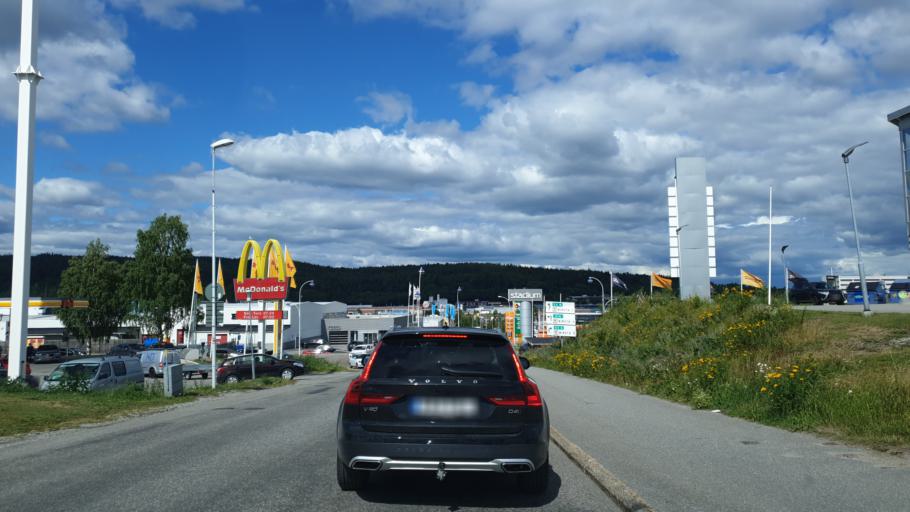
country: SE
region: Vaesternorrland
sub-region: Sundsvalls Kommun
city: Sundsbruk
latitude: 62.4410
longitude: 17.3315
